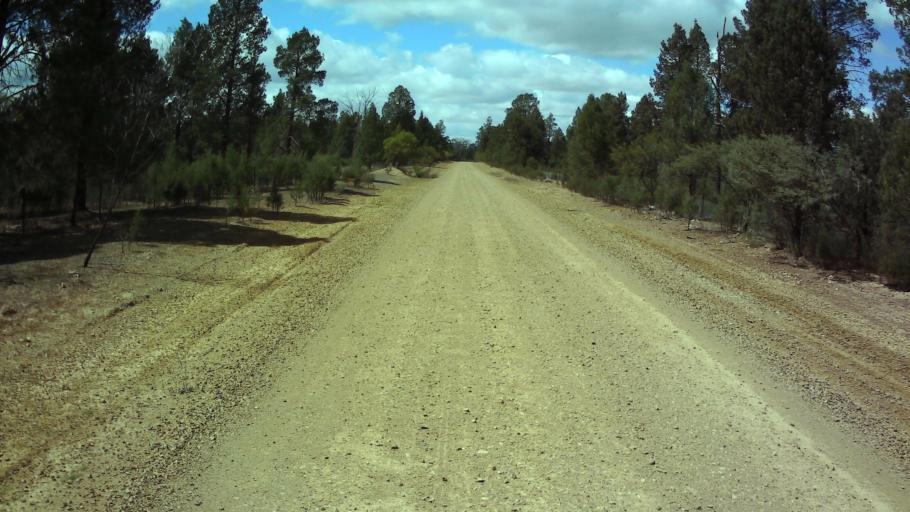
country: AU
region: New South Wales
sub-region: Weddin
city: Grenfell
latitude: -33.9111
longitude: 147.9199
